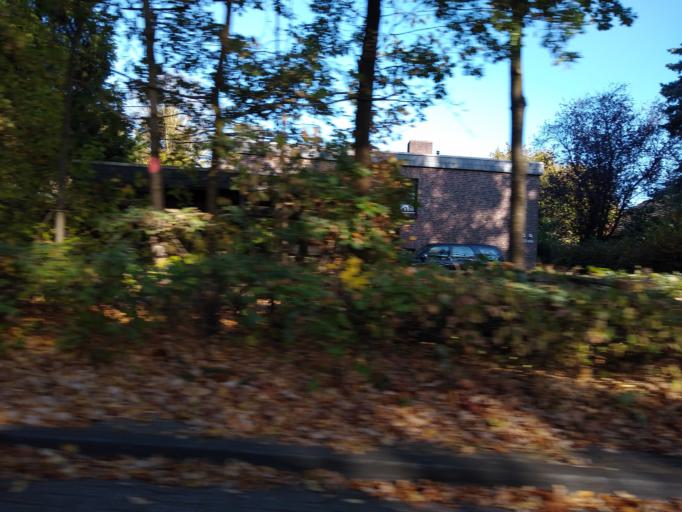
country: DE
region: Lower Saxony
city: Oldenburg
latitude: 53.1851
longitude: 8.2163
